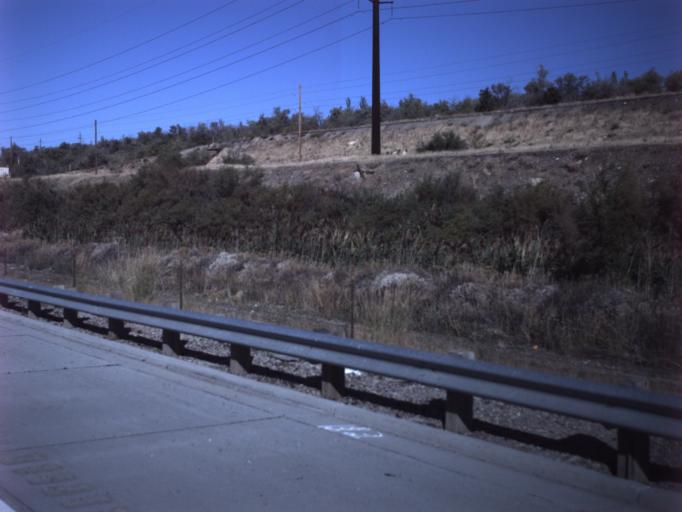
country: US
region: Utah
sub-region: Salt Lake County
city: Magna
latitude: 40.7182
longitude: -112.0995
